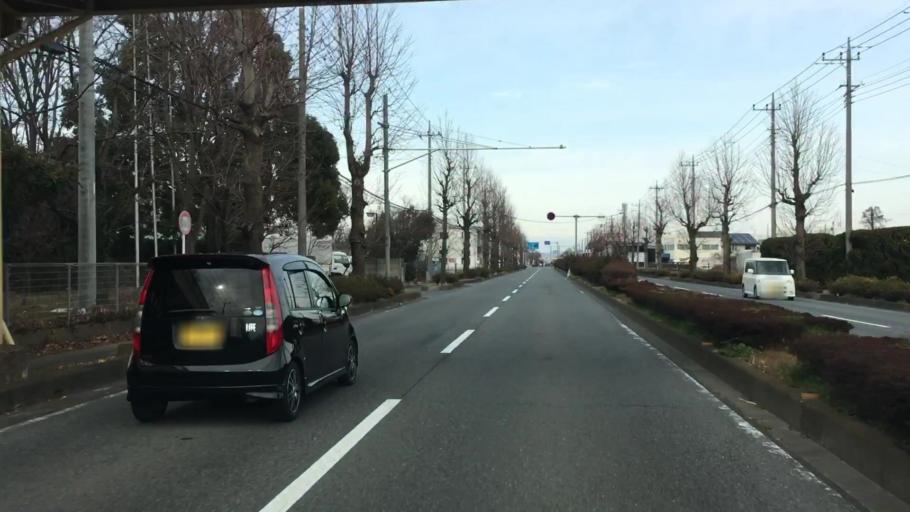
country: JP
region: Saitama
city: Menuma
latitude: 36.1831
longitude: 139.3700
